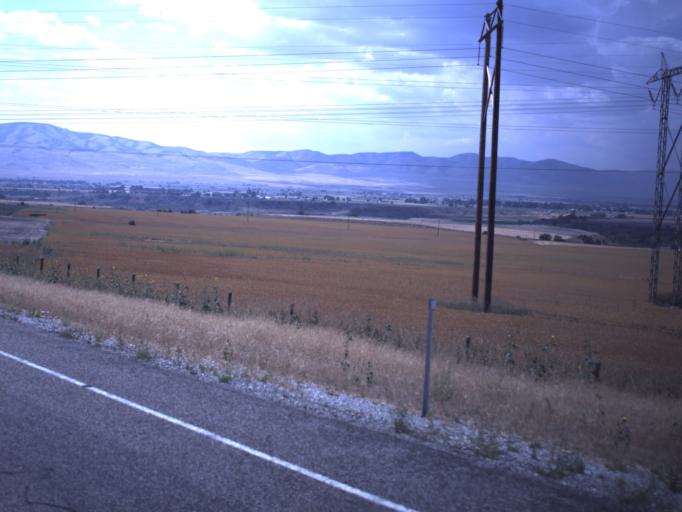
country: US
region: Utah
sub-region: Box Elder County
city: Garland
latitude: 41.7915
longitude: -112.0681
